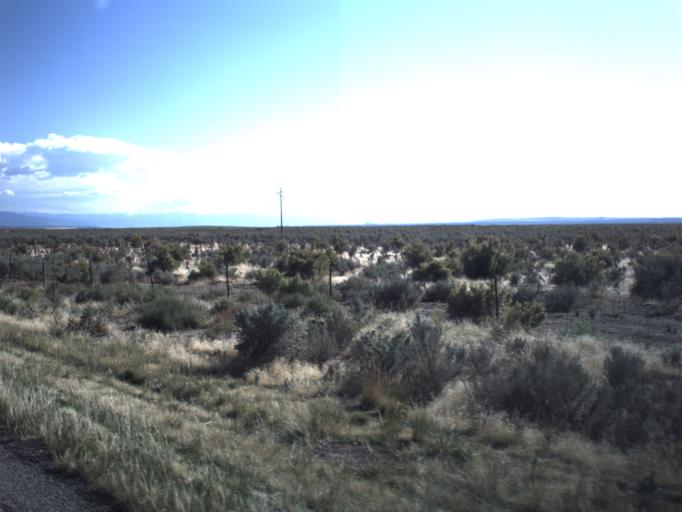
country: US
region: Utah
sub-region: Millard County
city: Delta
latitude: 39.2298
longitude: -112.4264
